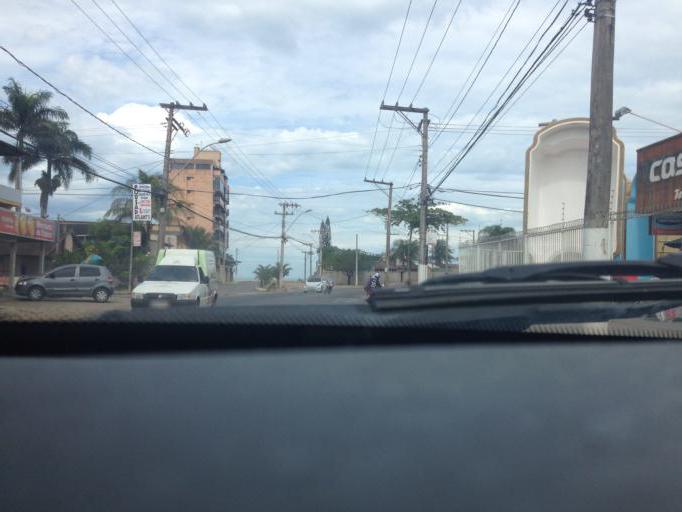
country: BR
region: Espirito Santo
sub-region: Guarapari
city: Guarapari
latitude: -20.6787
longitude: -40.5041
